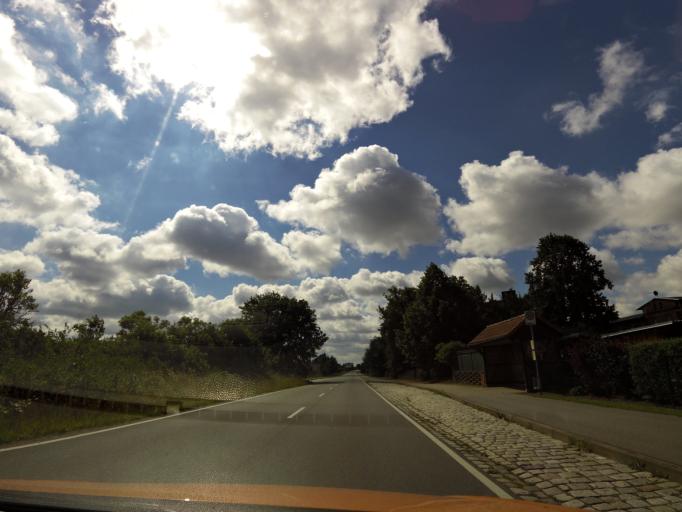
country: DE
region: Mecklenburg-Vorpommern
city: Plau am See
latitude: 53.5411
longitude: 12.2726
